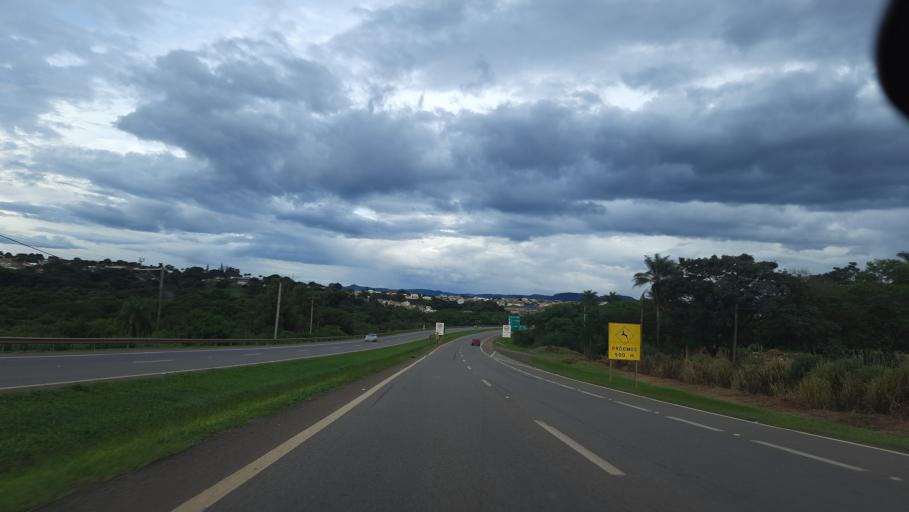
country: BR
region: Sao Paulo
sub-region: Sao Joao Da Boa Vista
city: Sao Joao da Boa Vista
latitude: -21.9934
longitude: -46.8042
